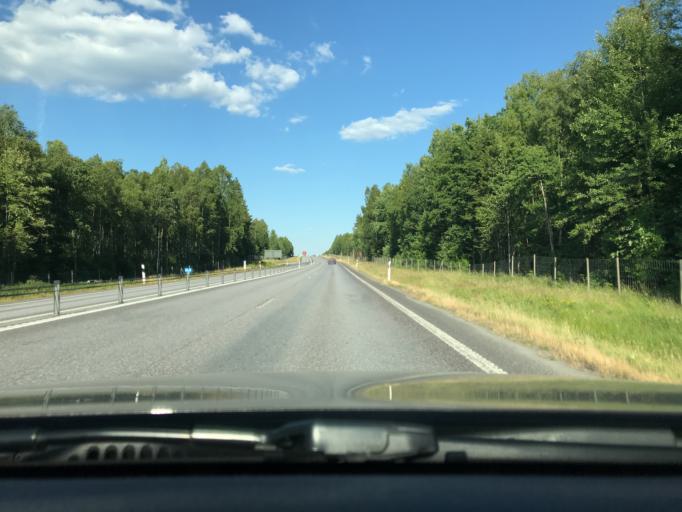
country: SE
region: Kronoberg
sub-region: Alvesta Kommun
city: Vislanda
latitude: 56.6999
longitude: 14.3562
